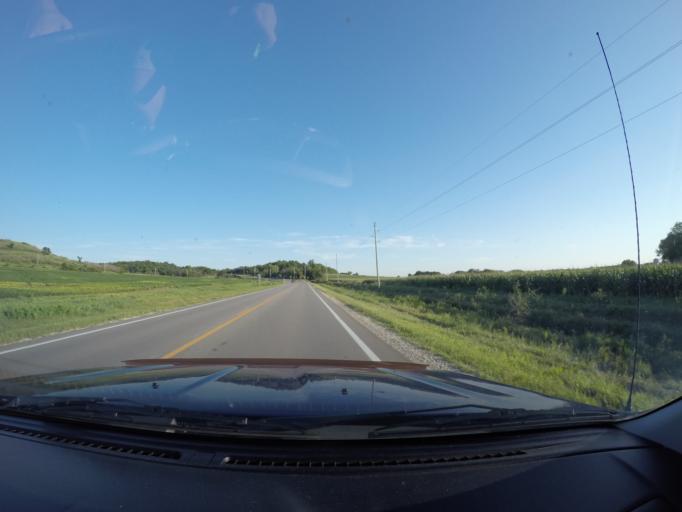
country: US
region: Kansas
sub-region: Pottawatomie County
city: Wamego
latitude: 39.1436
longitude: -96.3056
